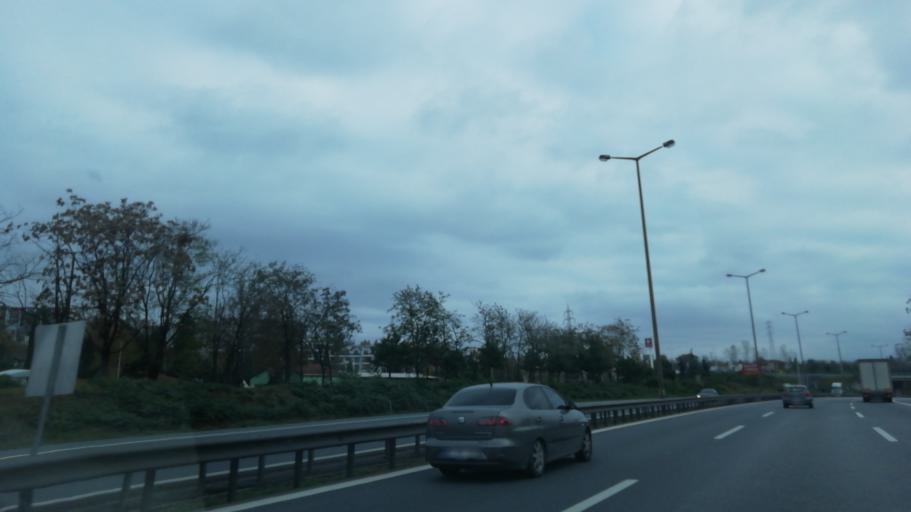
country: TR
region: Kocaeli
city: Izmit
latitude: 40.7820
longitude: 29.9266
